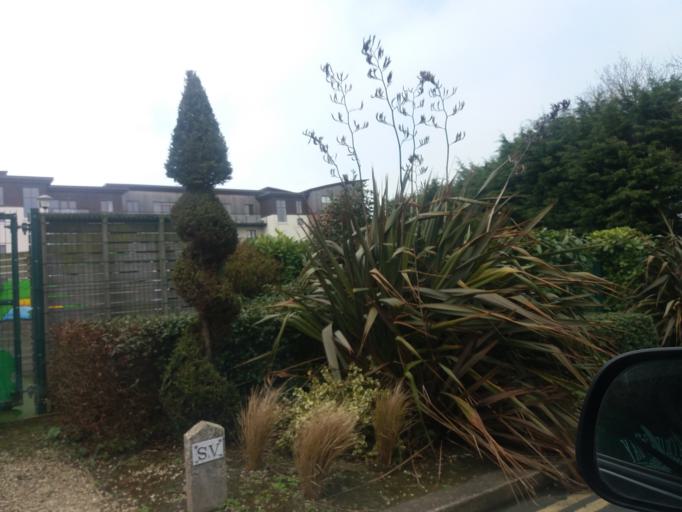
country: IE
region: Leinster
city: Portmarnock
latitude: 53.4196
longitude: -6.1504
